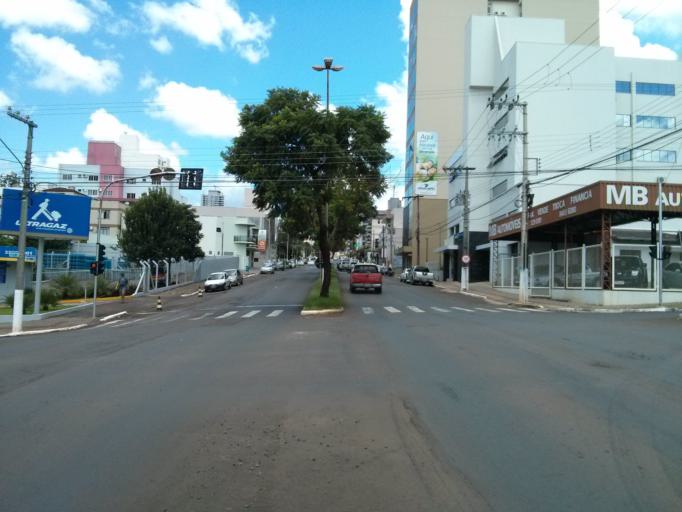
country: BR
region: Santa Catarina
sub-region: Chapeco
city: Chapeco
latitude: -27.1026
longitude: -52.6200
